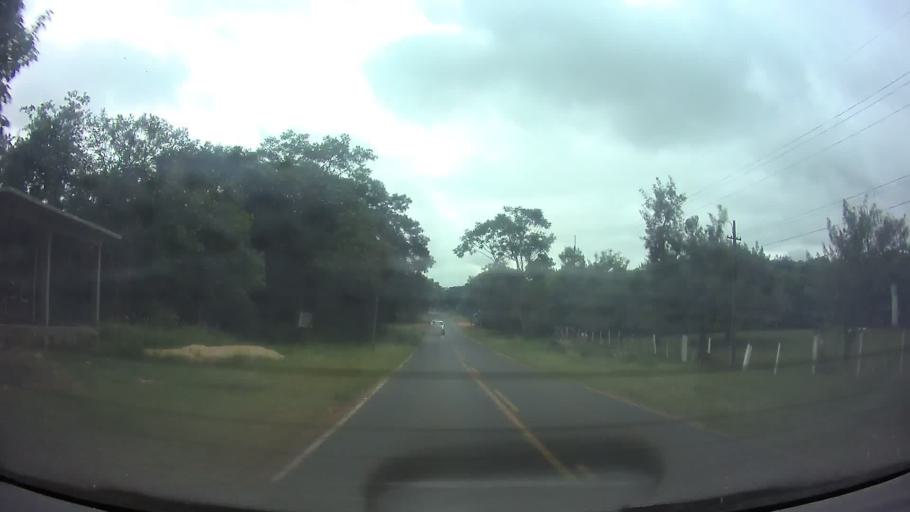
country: PY
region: Central
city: Guarambare
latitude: -25.5339
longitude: -57.5002
